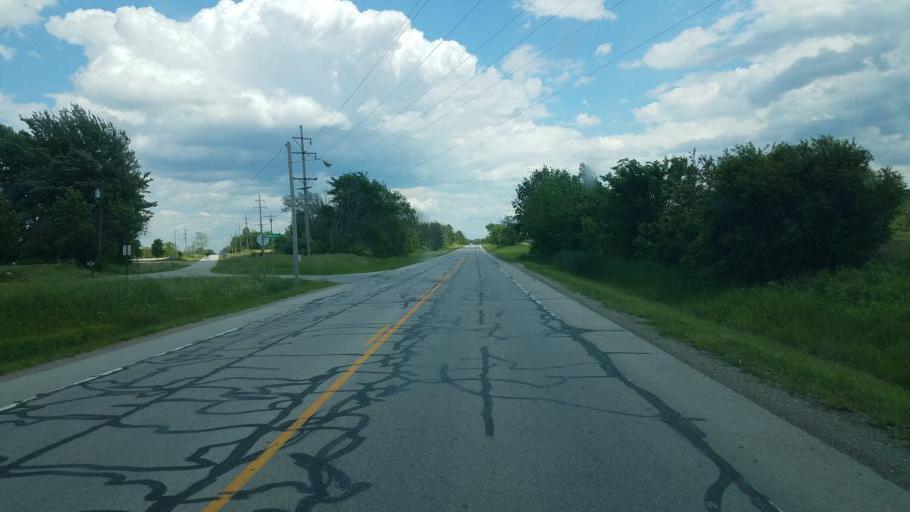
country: US
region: Ohio
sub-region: Crawford County
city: Crestline
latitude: 40.7842
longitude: -82.6812
